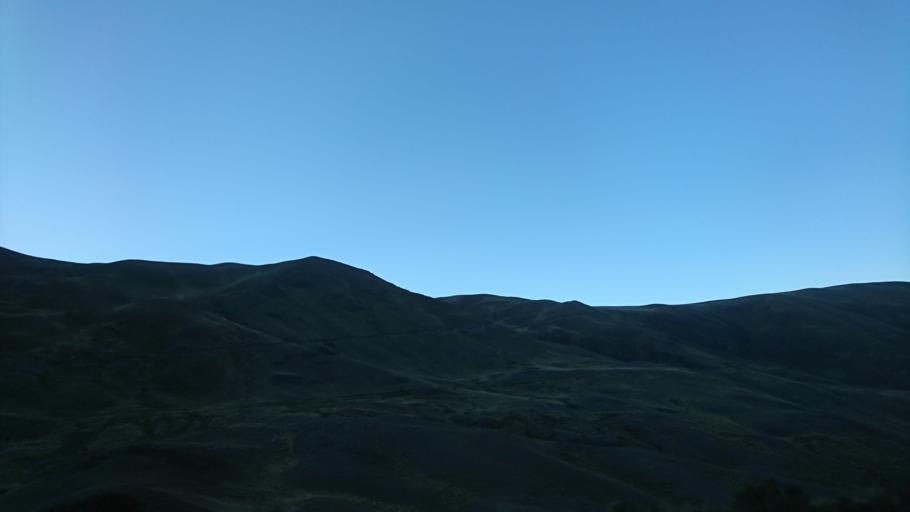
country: BO
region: La Paz
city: La Paz
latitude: -16.4124
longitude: -68.0519
